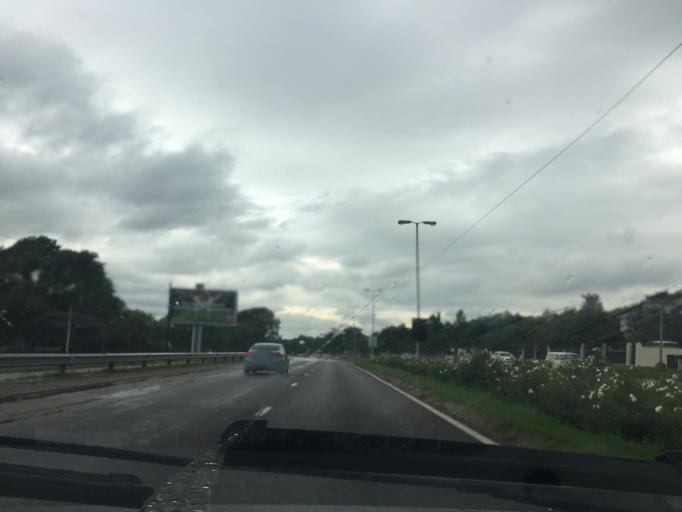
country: ZA
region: Gauteng
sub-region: City of Tshwane Metropolitan Municipality
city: Pretoria
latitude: -25.7671
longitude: 28.2991
